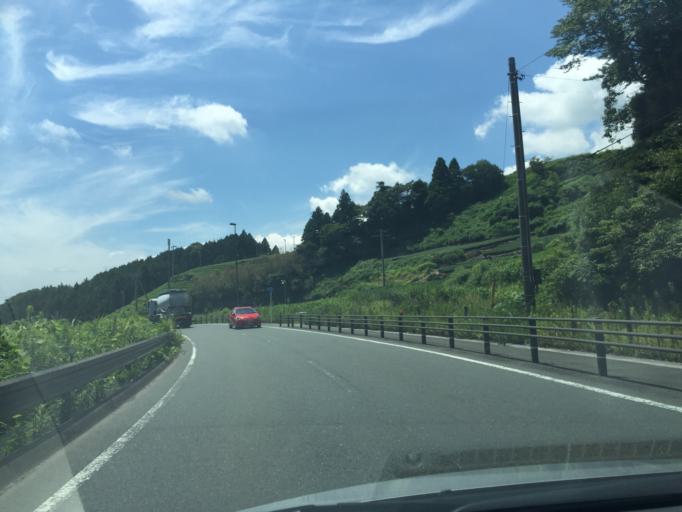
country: JP
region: Shizuoka
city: Kanaya
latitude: 34.8189
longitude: 138.0908
